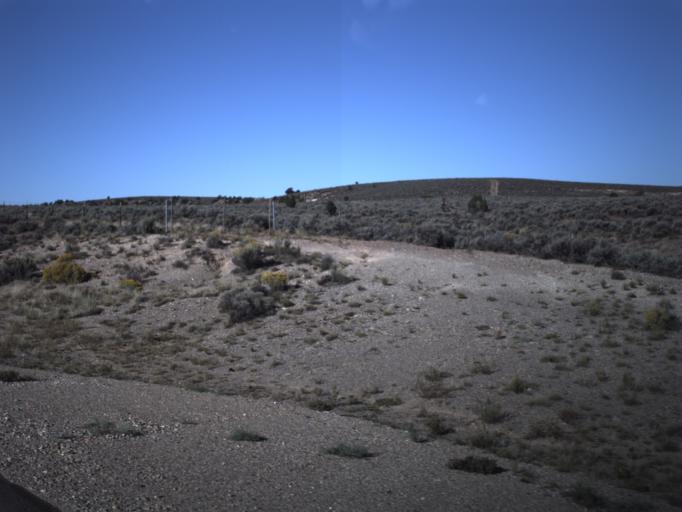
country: US
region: Utah
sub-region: Washington County
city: Enterprise
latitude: 37.7383
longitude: -114.0176
